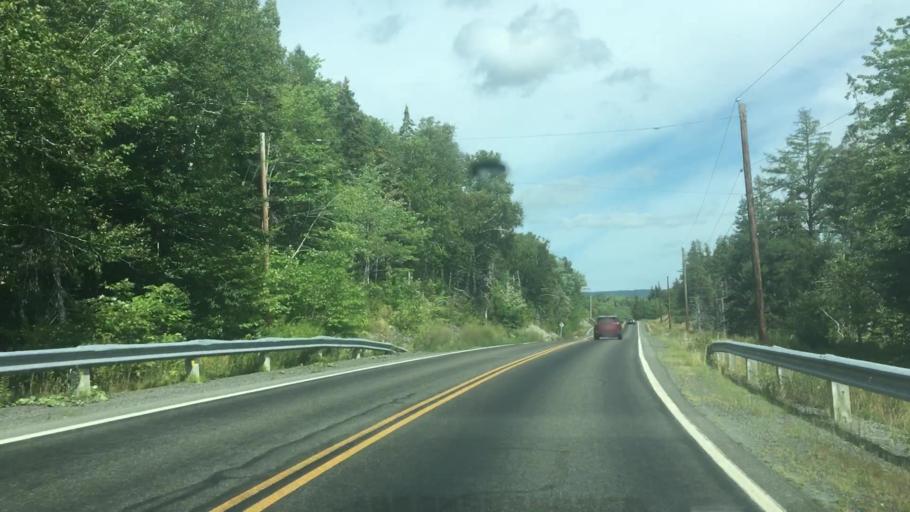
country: CA
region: Nova Scotia
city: Sydney Mines
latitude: 46.2148
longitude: -60.6202
